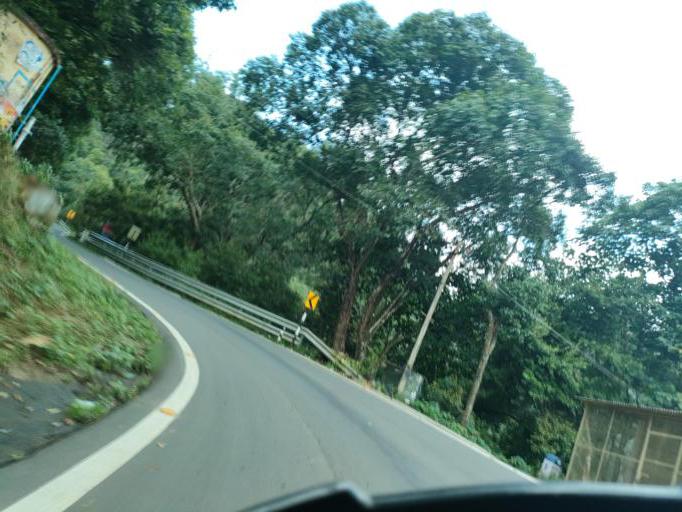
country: IN
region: Tamil Nadu
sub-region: Dindigul
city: Kodaikanal
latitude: 10.2664
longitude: 77.5342
